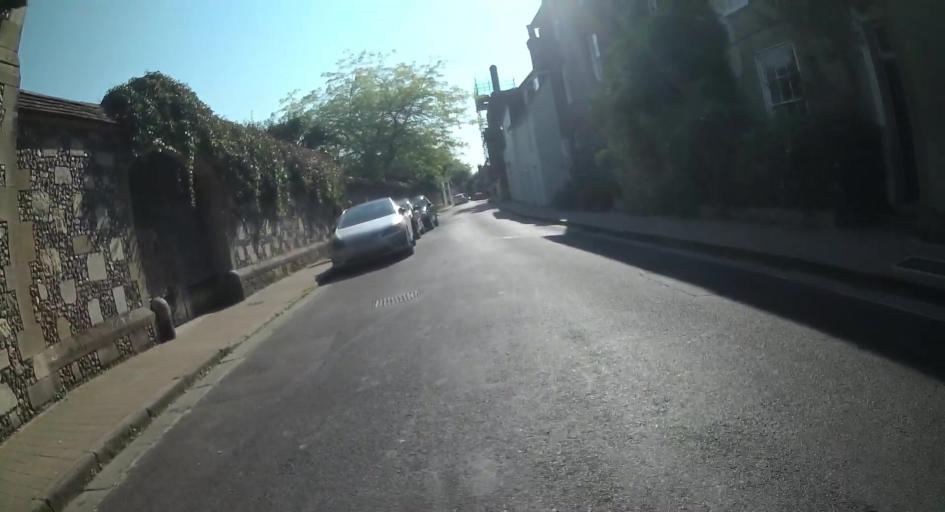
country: GB
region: England
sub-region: Hampshire
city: Winchester
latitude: 51.0570
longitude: -1.3156
